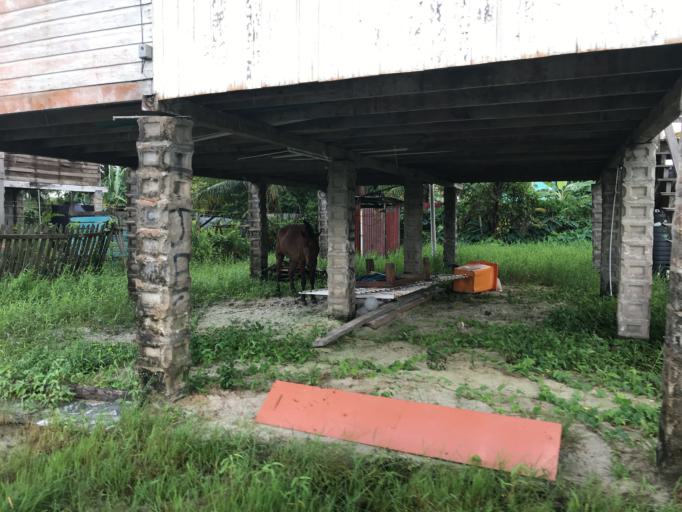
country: GY
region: Demerara-Mahaica
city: Georgetown
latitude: 6.8001
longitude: -58.1161
